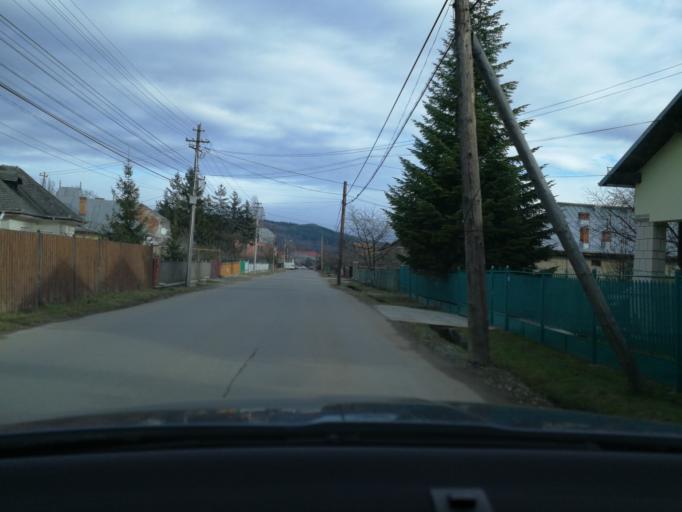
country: RO
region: Prahova
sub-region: Oras Breaza
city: Breaza
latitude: 45.1796
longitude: 25.6588
